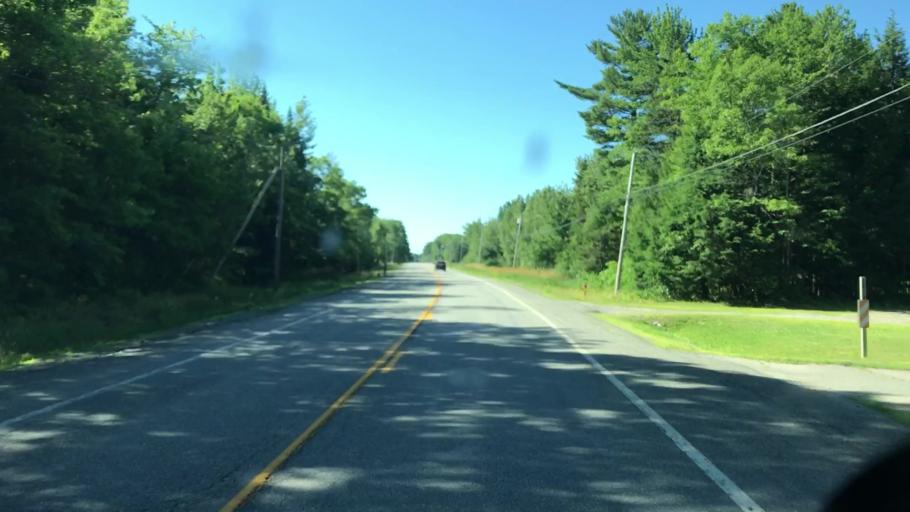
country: US
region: Maine
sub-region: Penobscot County
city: Howland
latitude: 45.2690
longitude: -68.6388
